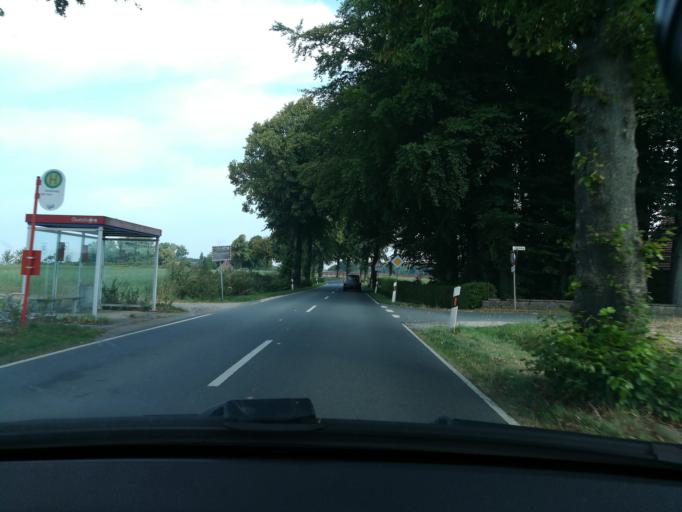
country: DE
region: Lower Saxony
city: Melle
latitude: 52.1500
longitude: 8.3333
